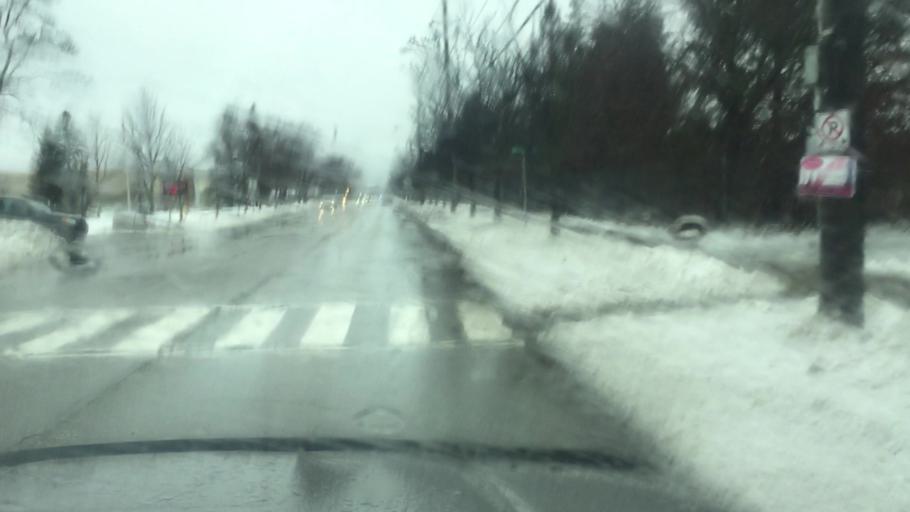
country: CA
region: Ontario
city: Ajax
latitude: 43.8579
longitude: -79.0570
